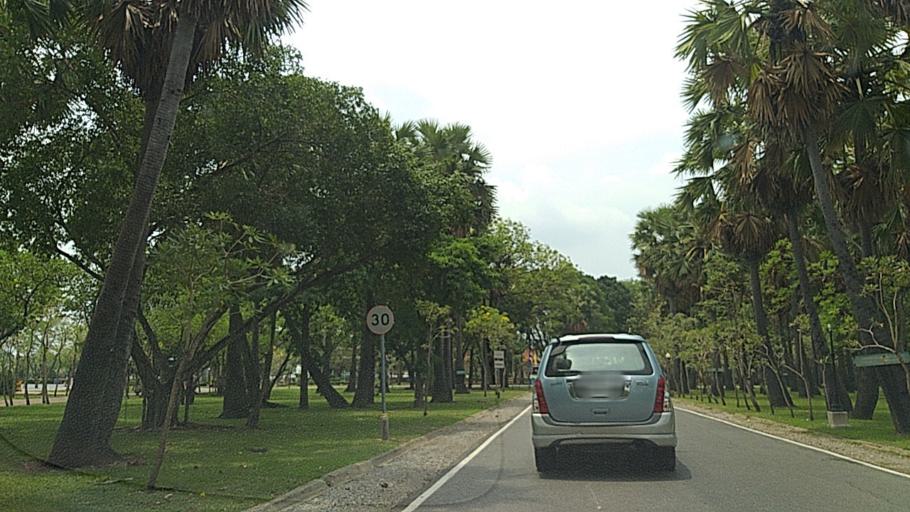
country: TH
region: Bangkok
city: Thawi Watthana
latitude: 13.7791
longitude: 100.3219
